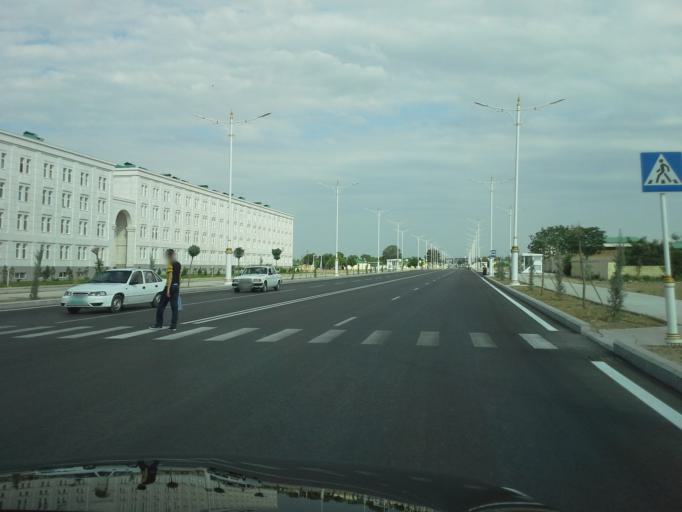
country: TM
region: Ahal
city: Ashgabat
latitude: 37.9642
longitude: 58.3299
